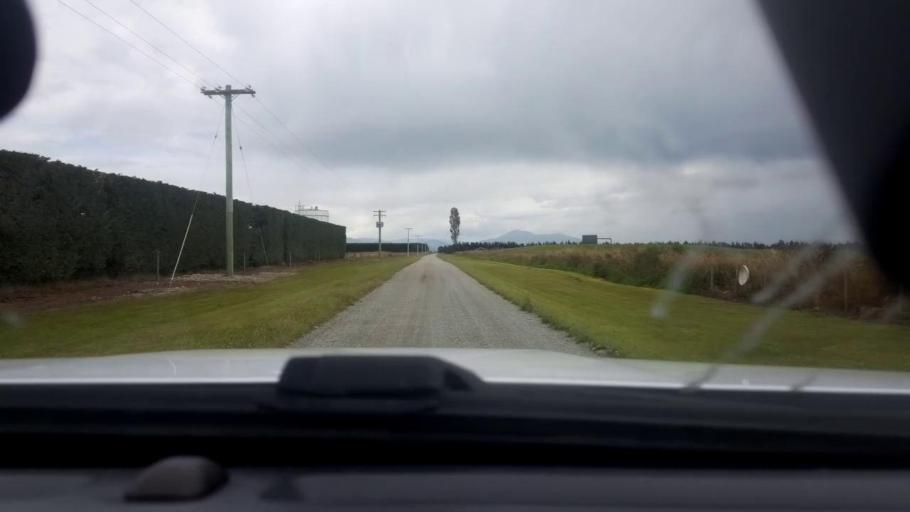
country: NZ
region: Canterbury
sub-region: Timaru District
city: Timaru
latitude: -44.1711
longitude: 171.4152
